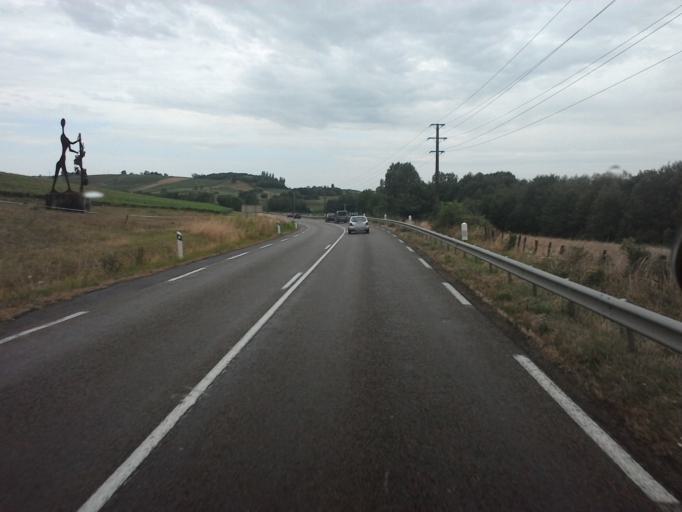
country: FR
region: Franche-Comte
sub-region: Departement du Jura
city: Arbois
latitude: 46.8973
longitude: 5.7396
